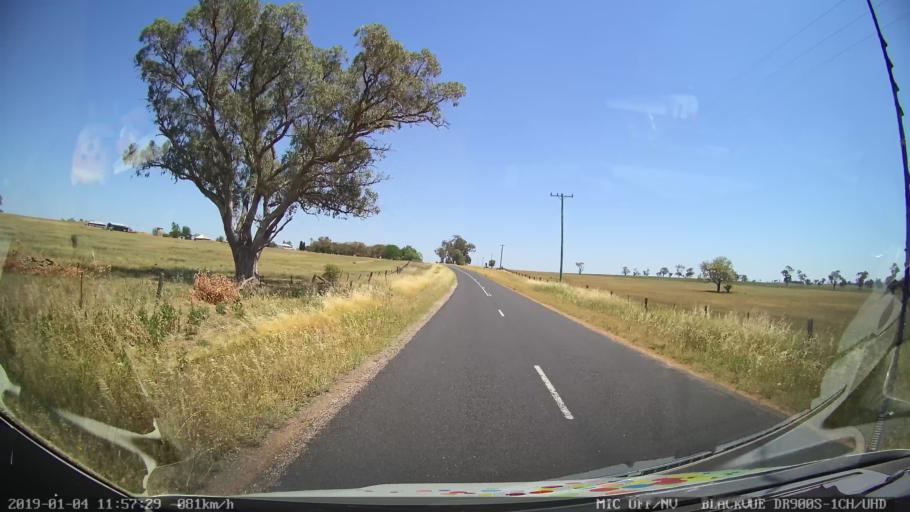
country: AU
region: New South Wales
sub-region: Cabonne
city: Molong
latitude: -32.8348
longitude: 148.7071
